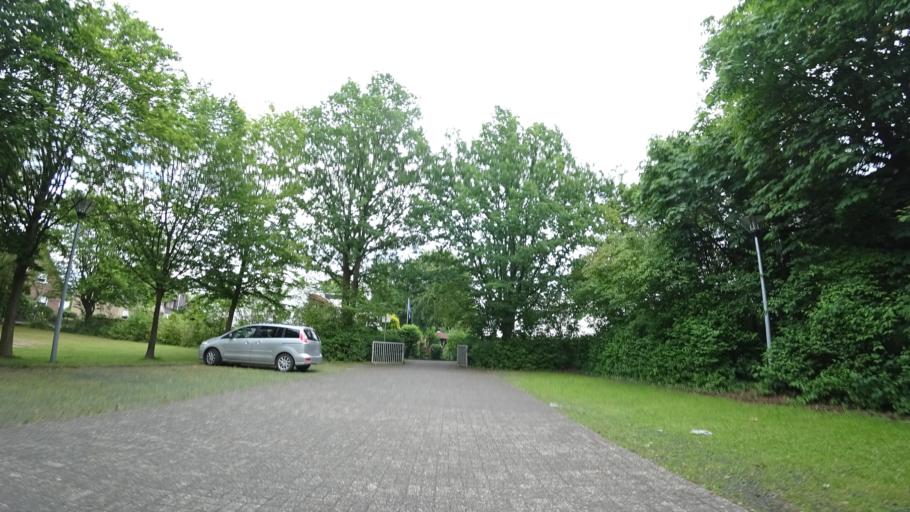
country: DE
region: North Rhine-Westphalia
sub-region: Regierungsbezirk Detmold
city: Guetersloh
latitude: 51.9320
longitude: 8.3638
